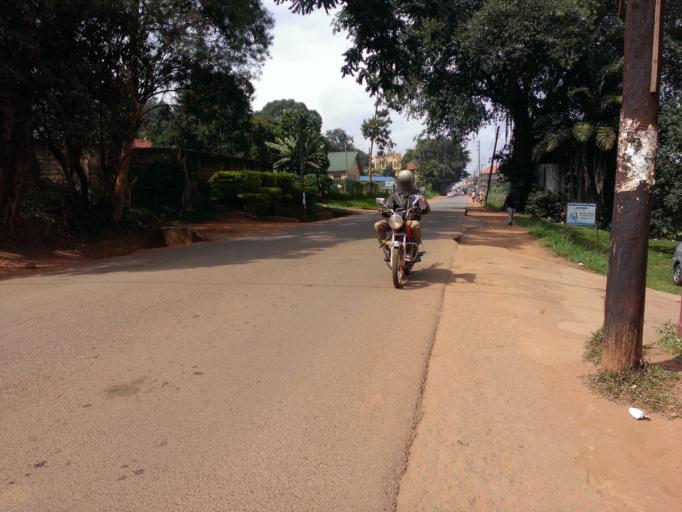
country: UG
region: Central Region
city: Kampala Central Division
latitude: 0.3174
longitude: 32.5576
